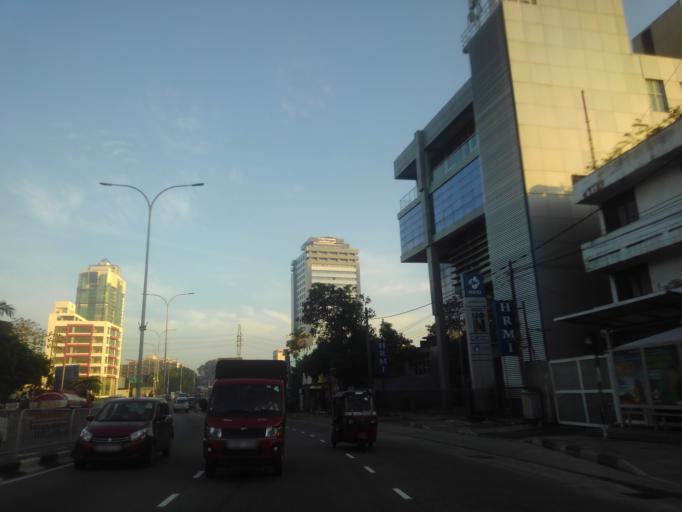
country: LK
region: Western
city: Pita Kotte
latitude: 6.8867
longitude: 79.8772
